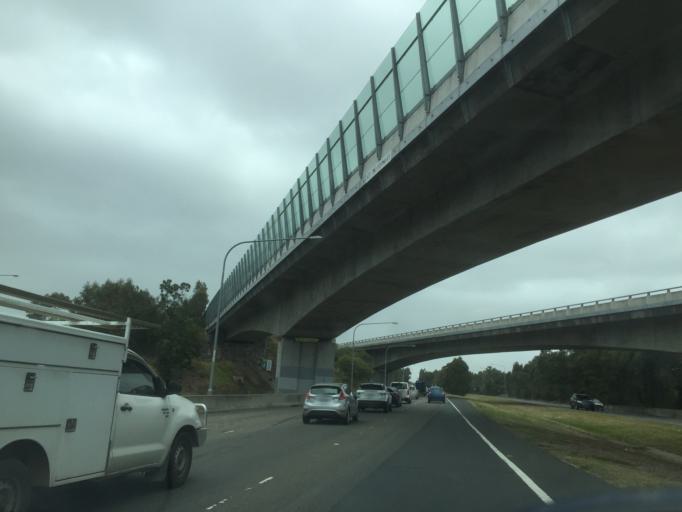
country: AU
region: New South Wales
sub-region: Blacktown
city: Blacktown
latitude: -33.7527
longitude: 150.9523
